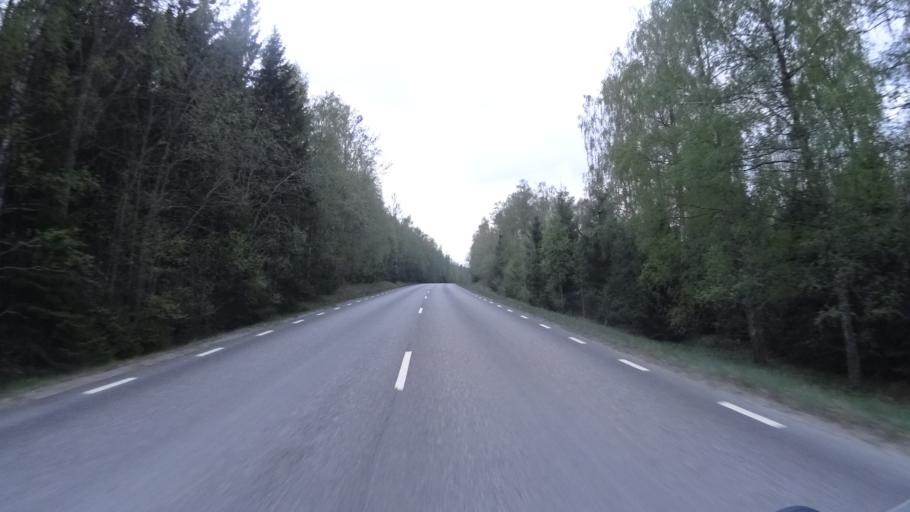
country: SE
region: Vaestra Goetaland
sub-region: Gotene Kommun
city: Goetene
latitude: 58.6110
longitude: 13.4014
